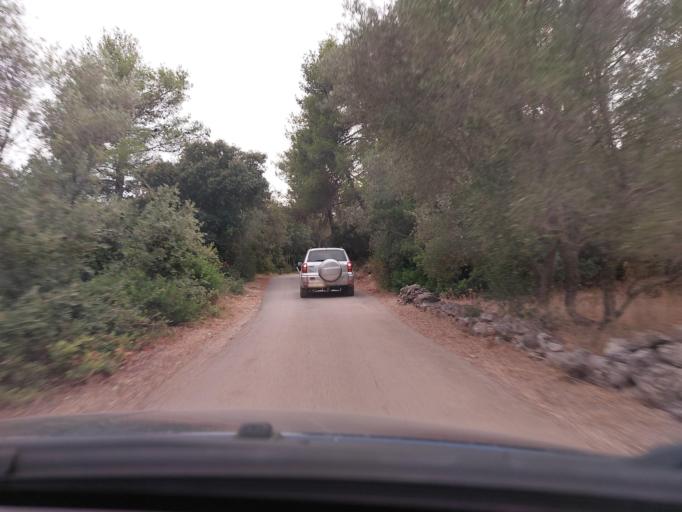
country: HR
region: Dubrovacko-Neretvanska
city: Smokvica
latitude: 42.7619
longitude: 16.9047
